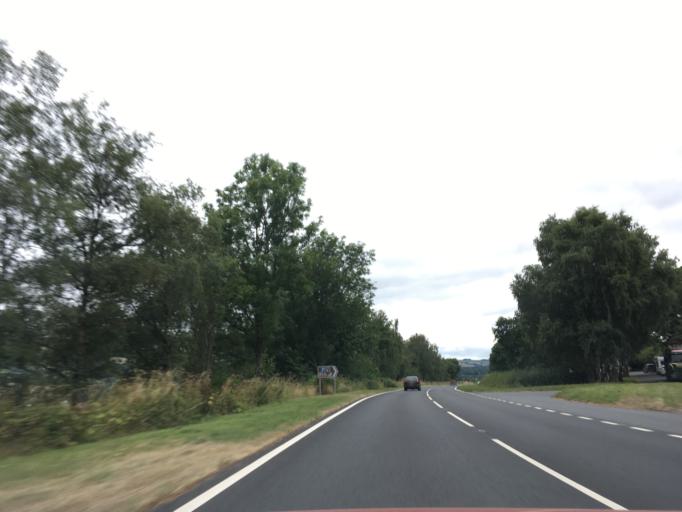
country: GB
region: Wales
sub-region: Blaenau Gwent
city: Tredegar
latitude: 51.8948
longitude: -3.2640
